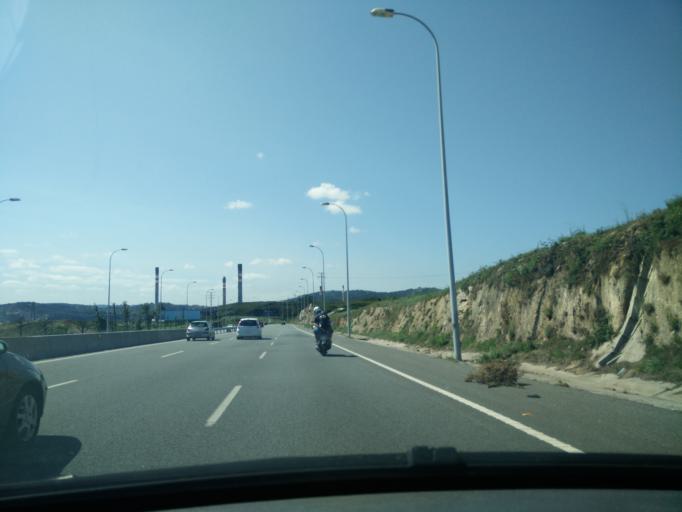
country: ES
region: Galicia
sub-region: Provincia da Coruna
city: A Coruna
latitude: 43.3582
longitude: -8.4340
